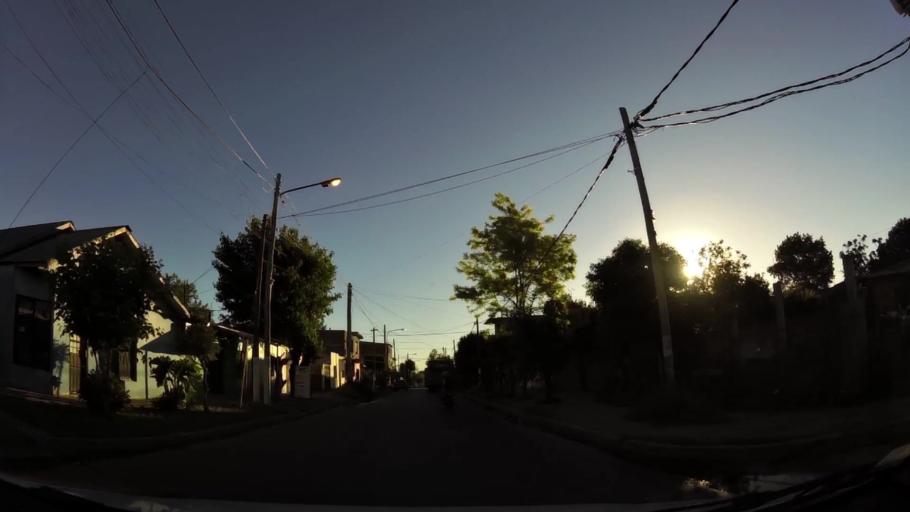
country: AR
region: Buenos Aires
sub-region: Partido de Moron
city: Moron
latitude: -34.7153
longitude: -58.6147
